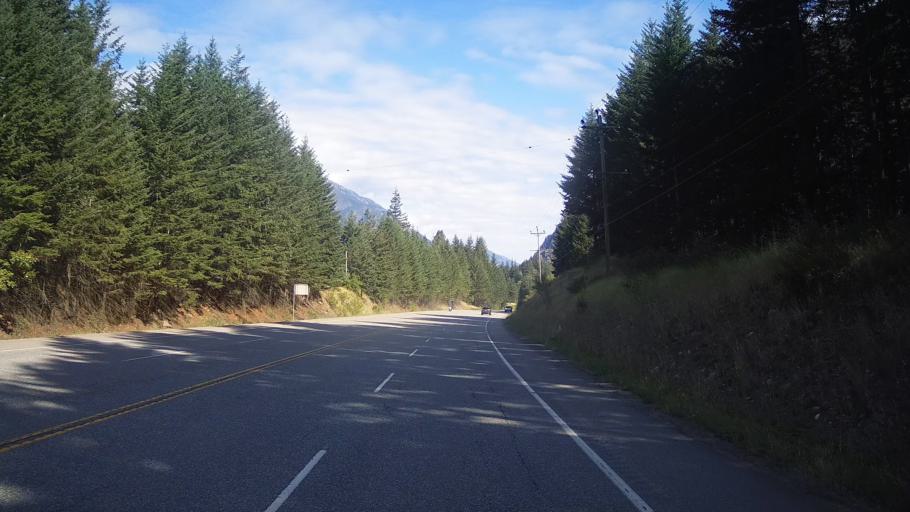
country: CA
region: British Columbia
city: Hope
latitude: 50.0491
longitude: -121.5404
